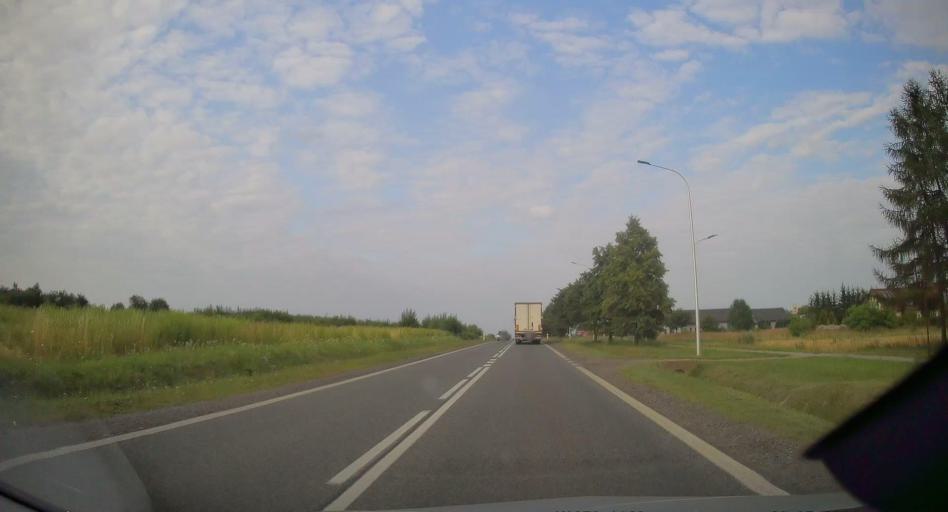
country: PL
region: Silesian Voivodeship
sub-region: Powiat czestochowski
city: Rudniki
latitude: 50.8702
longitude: 19.2339
